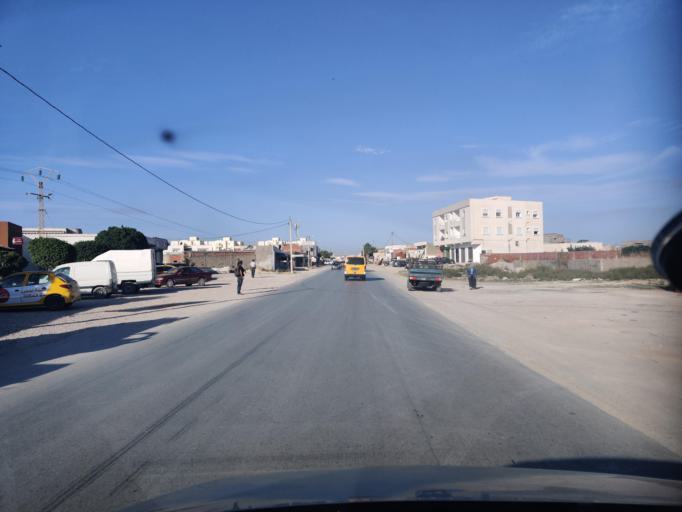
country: TN
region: Ariana
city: Ariana
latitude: 36.9562
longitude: 10.2214
